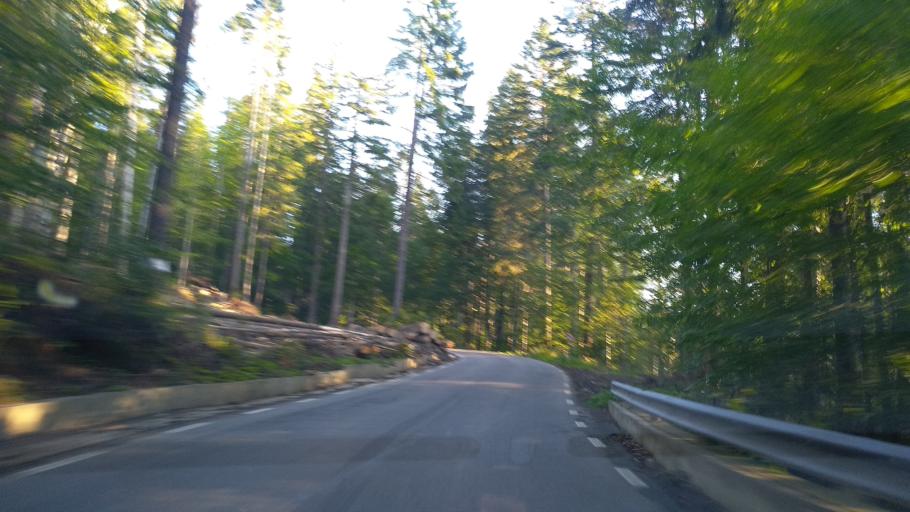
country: RO
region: Prahova
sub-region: Oras Sinaia
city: Sinaia
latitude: 45.3134
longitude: 25.5205
